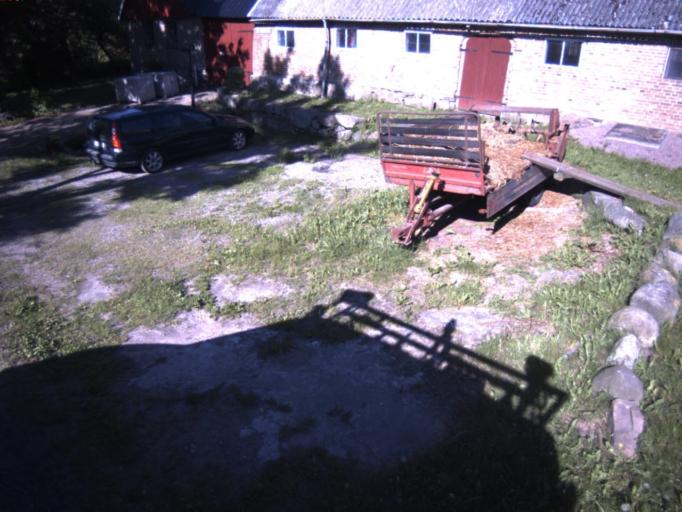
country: SE
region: Skane
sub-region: Helsingborg
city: Gantofta
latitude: 55.9903
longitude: 12.7834
